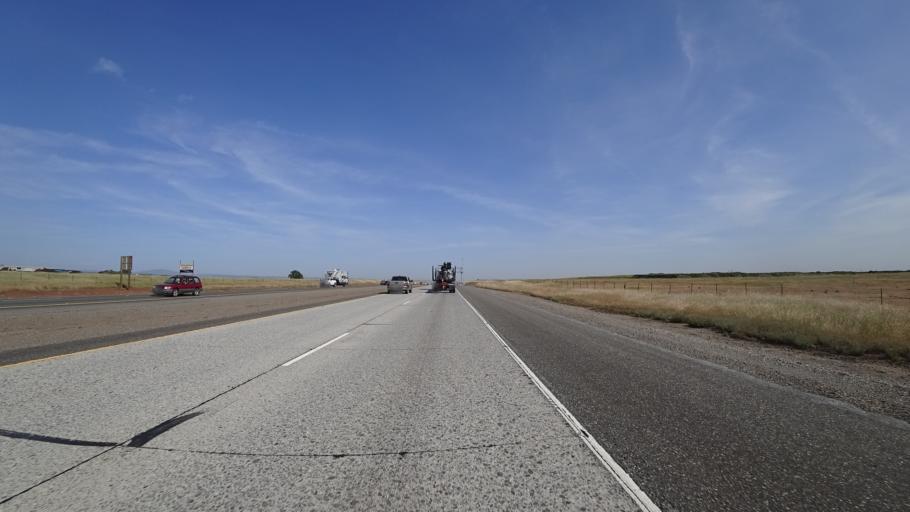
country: US
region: California
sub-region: Butte County
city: Durham
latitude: 39.6633
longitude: -121.7409
